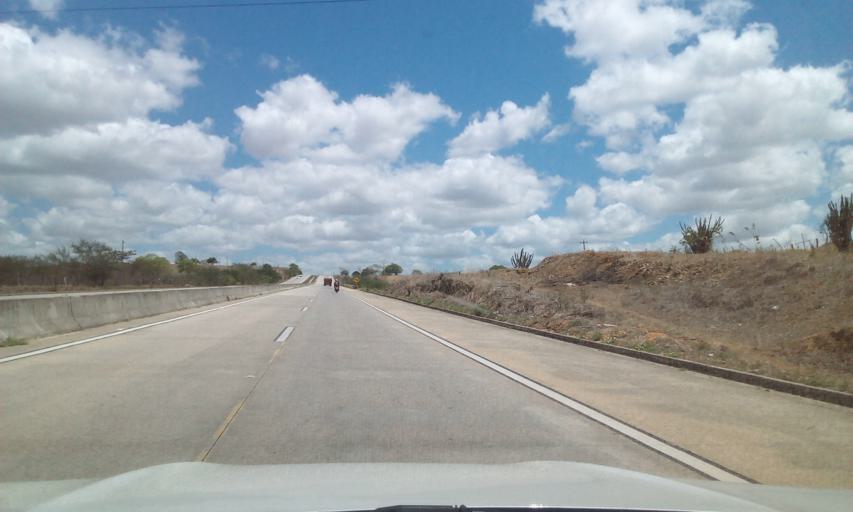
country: BR
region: Alagoas
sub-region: Porto Real Do Colegio
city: Porto Real do Colegio
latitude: -10.1421
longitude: -36.8043
